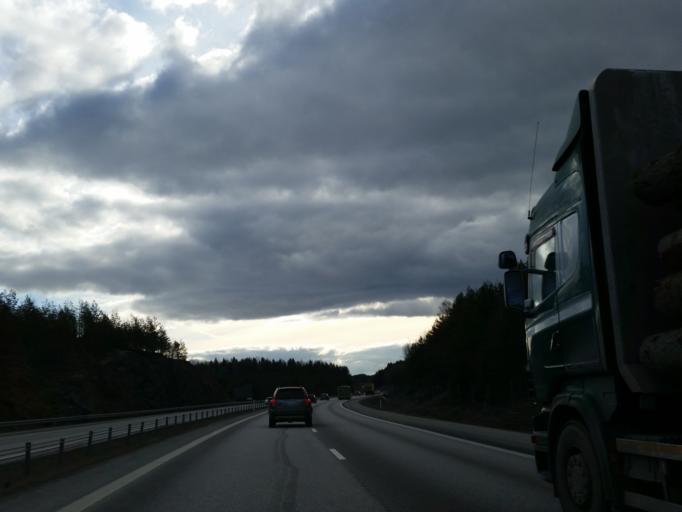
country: SE
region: Soedermanland
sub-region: Oxelosunds Kommun
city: Oxelosund
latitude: 58.8519
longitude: 17.2040
